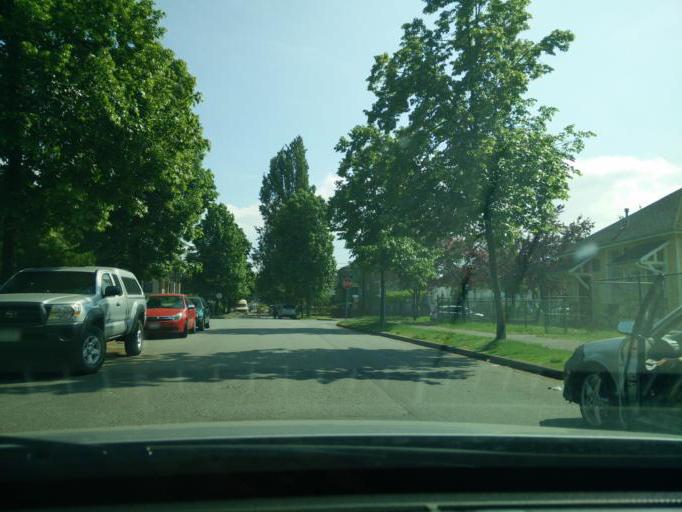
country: CA
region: British Columbia
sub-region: Fraser Valley Regional District
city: North Vancouver
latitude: 49.2807
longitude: -123.0637
